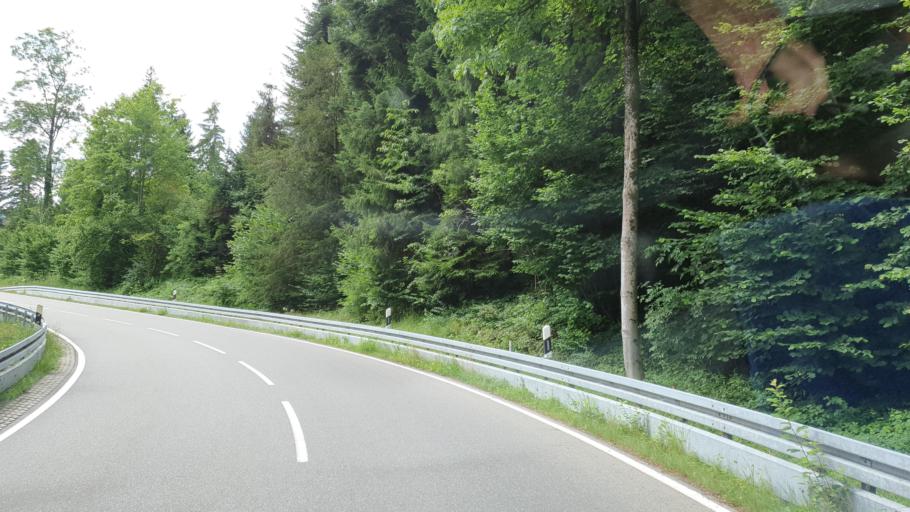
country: DE
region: Bavaria
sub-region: Swabia
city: Scheidegg
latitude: 47.5942
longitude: 9.8367
